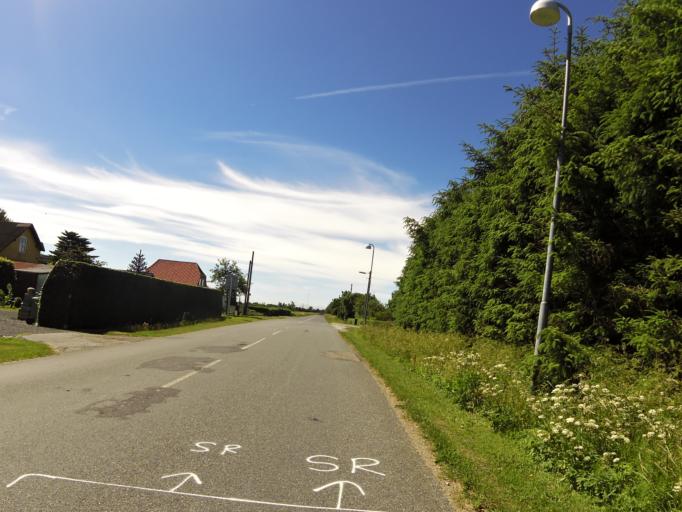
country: DK
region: South Denmark
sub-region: Aabenraa Kommune
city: Rodekro
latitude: 55.0341
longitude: 9.3028
